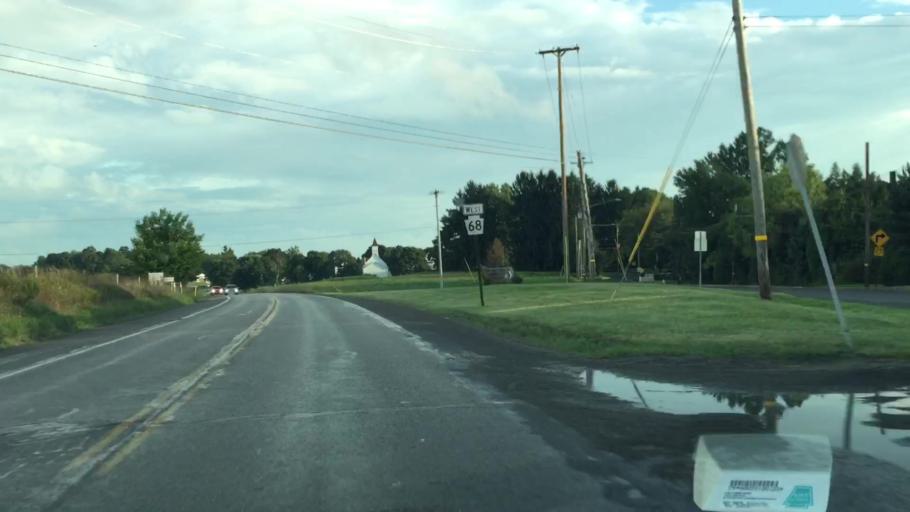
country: US
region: Pennsylvania
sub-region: Butler County
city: Meridian
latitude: 40.8222
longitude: -80.0114
